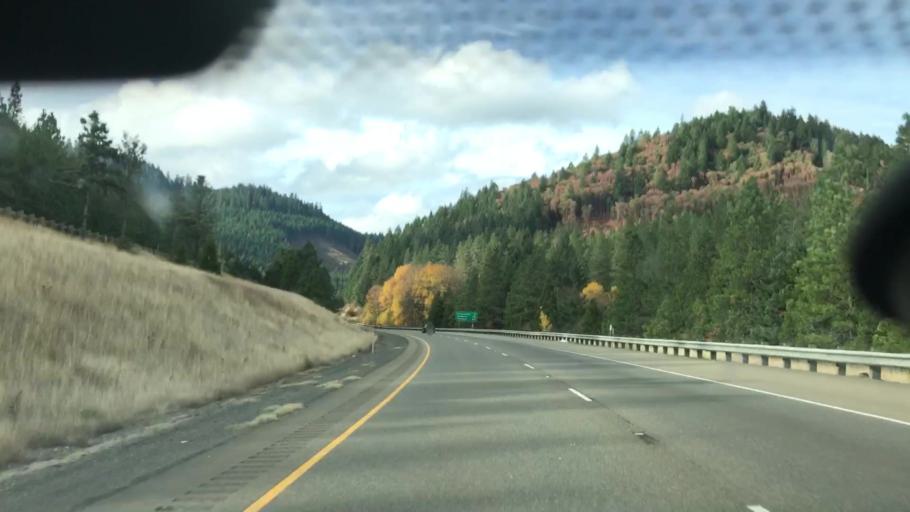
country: US
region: Oregon
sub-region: Douglas County
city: Canyonville
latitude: 42.8076
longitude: -123.2534
